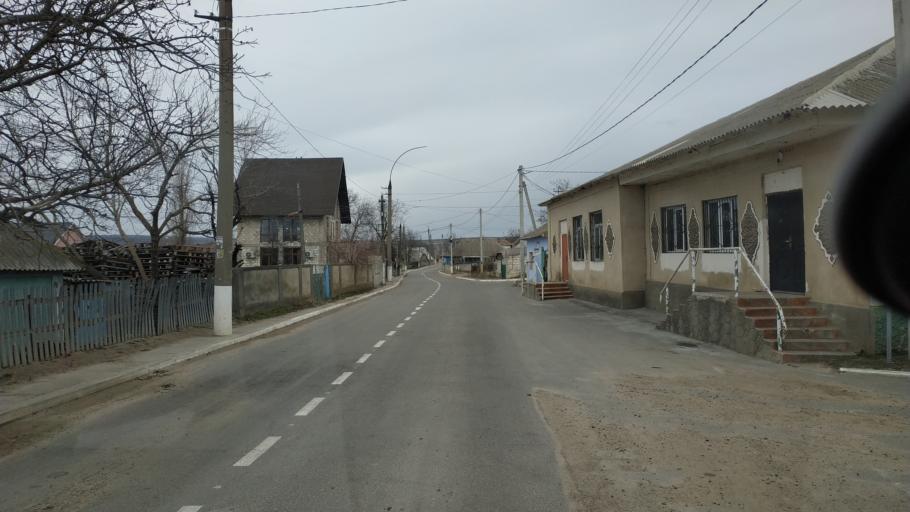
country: MD
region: Telenesti
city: Cocieri
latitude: 47.3472
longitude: 29.1108
